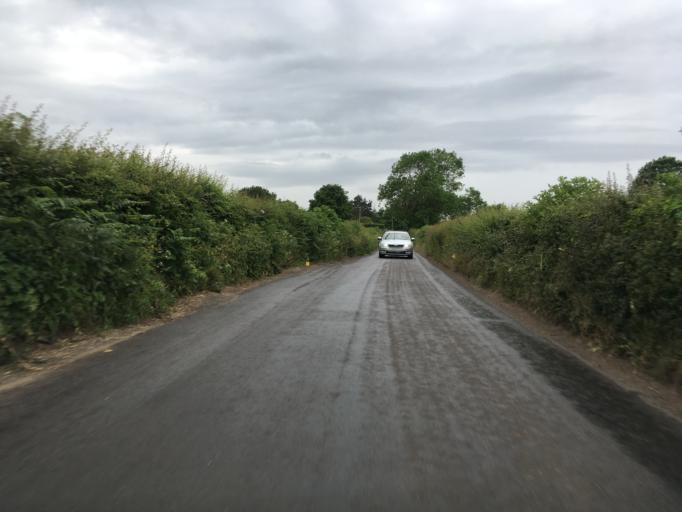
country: GB
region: England
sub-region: North Somerset
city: Brockley
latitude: 51.4136
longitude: -2.7860
